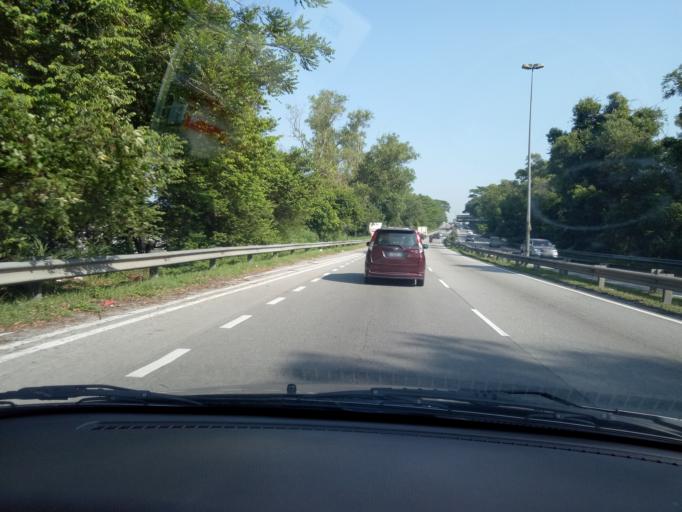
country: MY
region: Selangor
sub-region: Hulu Langat
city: Semenyih
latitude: 2.9995
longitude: 101.8106
